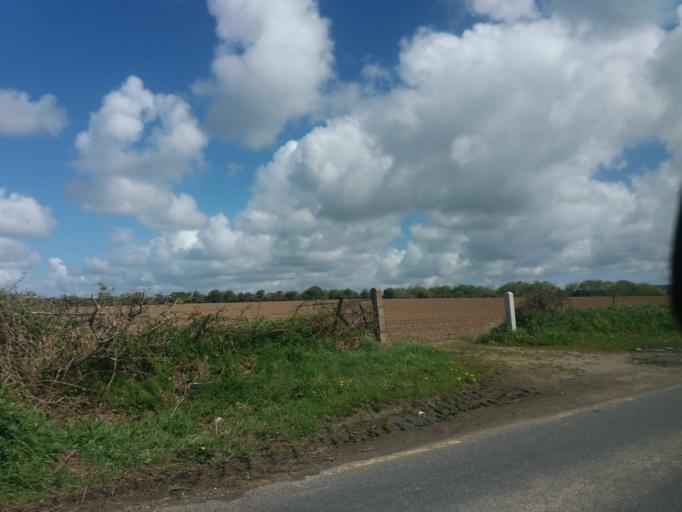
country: IE
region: Leinster
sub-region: Loch Garman
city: Loch Garman
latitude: 52.2828
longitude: -6.6599
